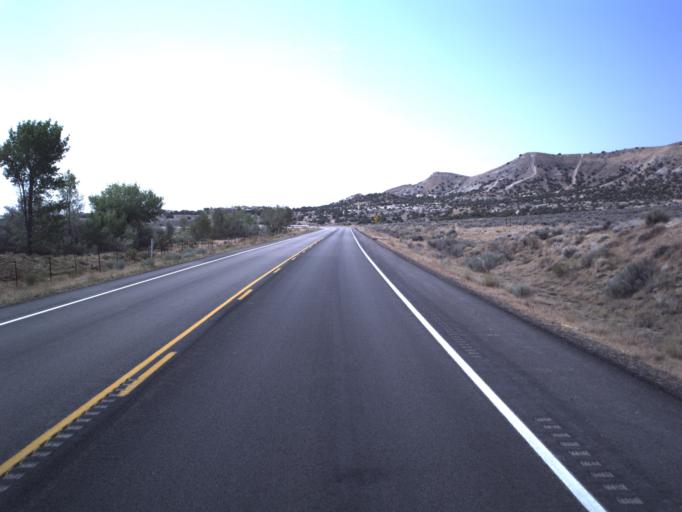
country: US
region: Utah
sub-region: Uintah County
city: Naples
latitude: 40.3609
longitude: -109.4982
